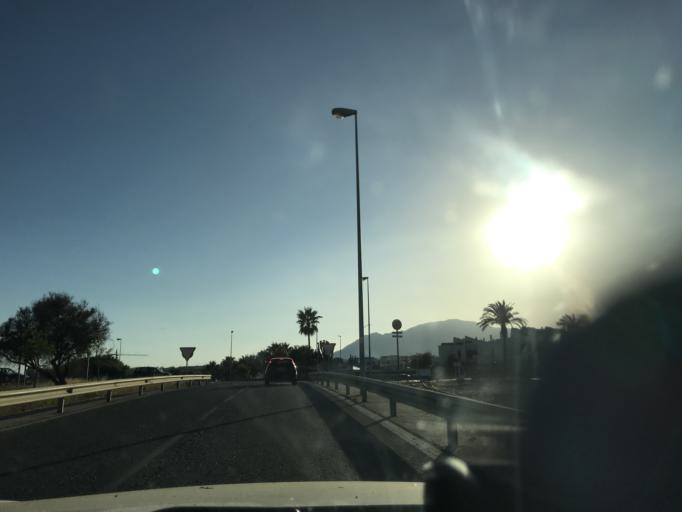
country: ES
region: Andalusia
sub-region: Provincia de Malaga
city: Benahavis
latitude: 36.4620
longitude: -5.0455
